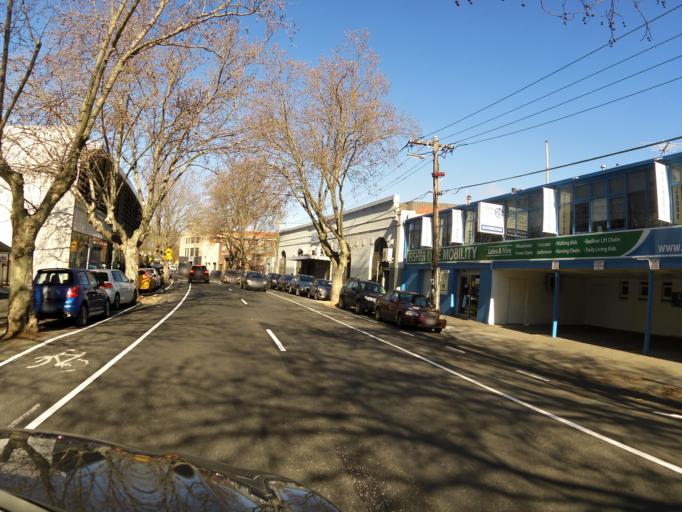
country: AU
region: Victoria
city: Abbotsford
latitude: -37.8061
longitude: 144.9981
